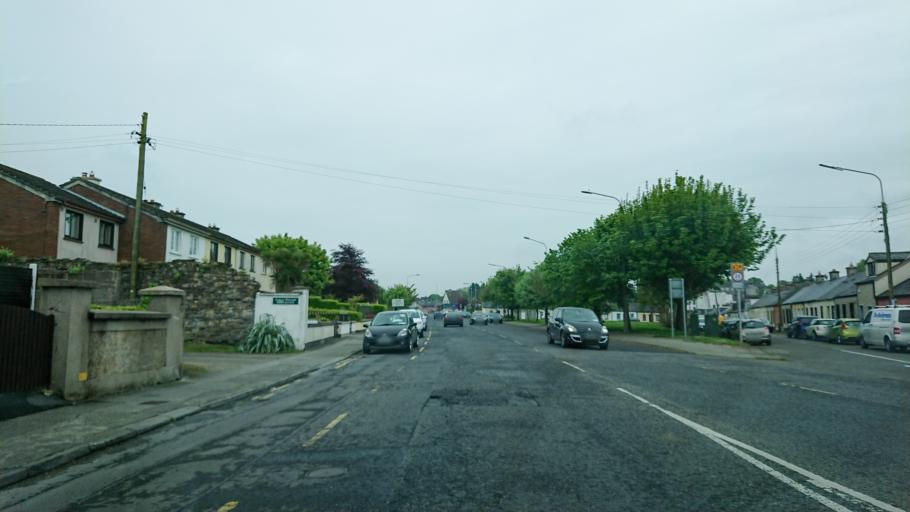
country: IE
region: Munster
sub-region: Waterford
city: Waterford
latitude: 52.2496
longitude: -7.1107
